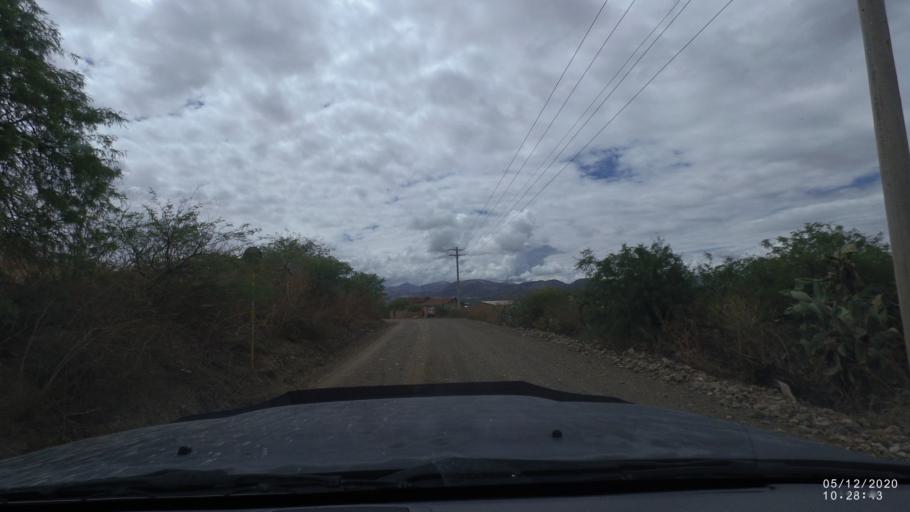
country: BO
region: Cochabamba
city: Sipe Sipe
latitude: -17.5393
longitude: -66.2715
